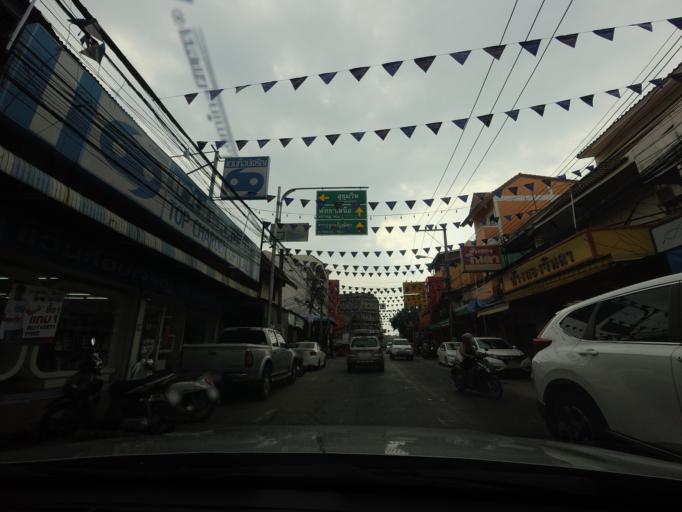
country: TH
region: Chon Buri
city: Phatthaya
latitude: 12.9736
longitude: 100.9071
